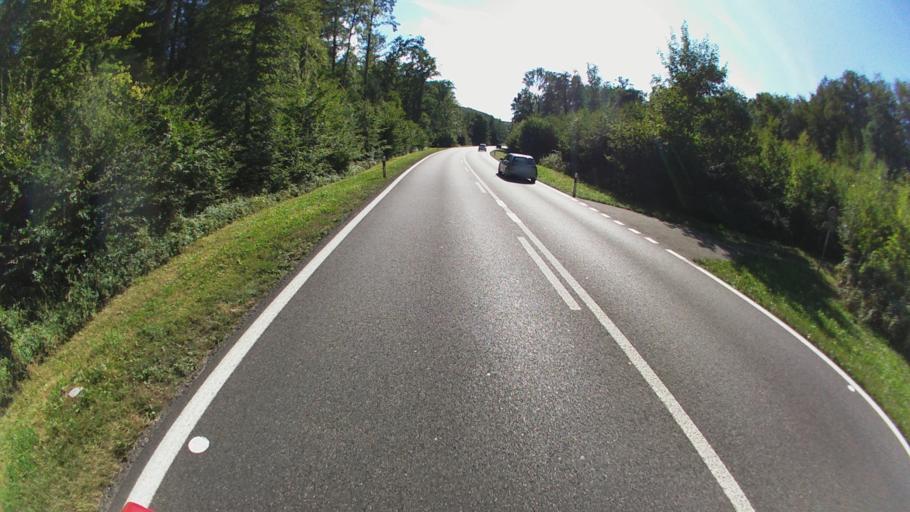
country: DE
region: Baden-Wuerttemberg
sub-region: Freiburg Region
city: Murg
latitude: 47.5421
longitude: 8.0087
